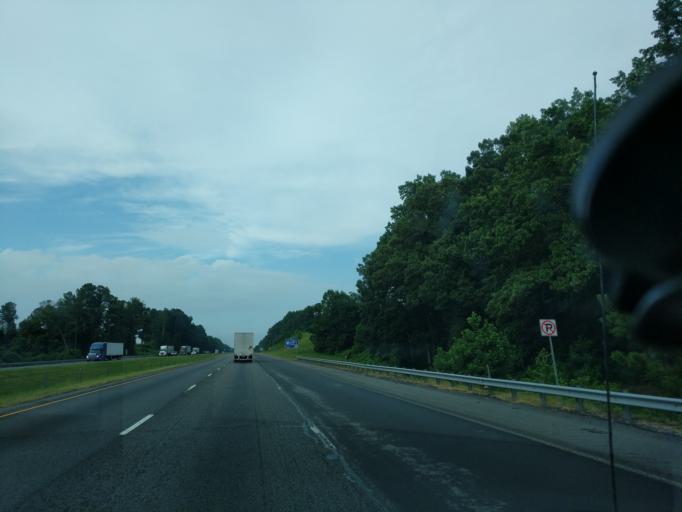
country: US
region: Georgia
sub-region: Franklin County
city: Lavonia
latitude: 34.4311
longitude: -83.1510
